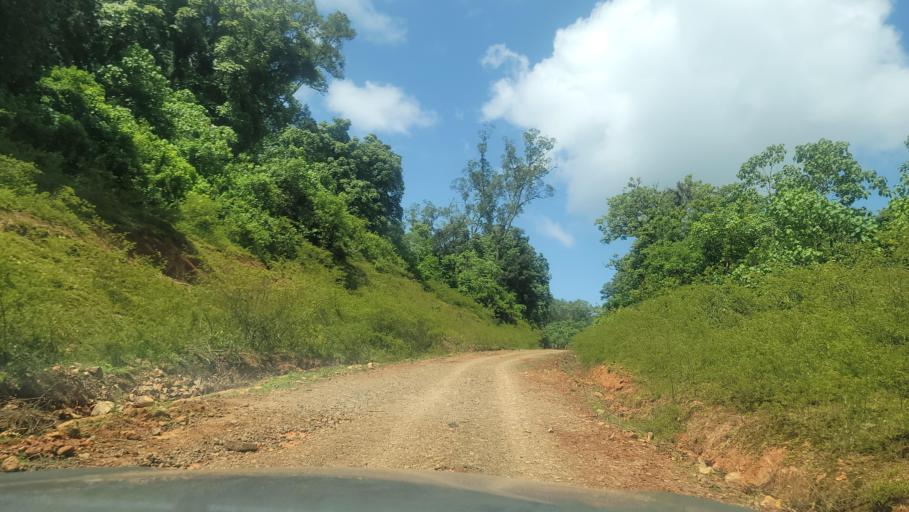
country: ET
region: Southern Nations, Nationalities, and People's Region
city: Bonga
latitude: 7.6850
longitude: 36.2401
